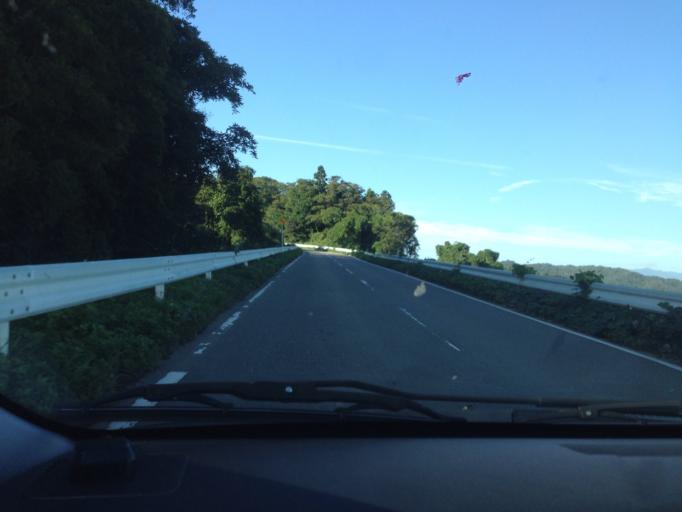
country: JP
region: Fukushima
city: Kitakata
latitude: 37.5914
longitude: 139.8130
